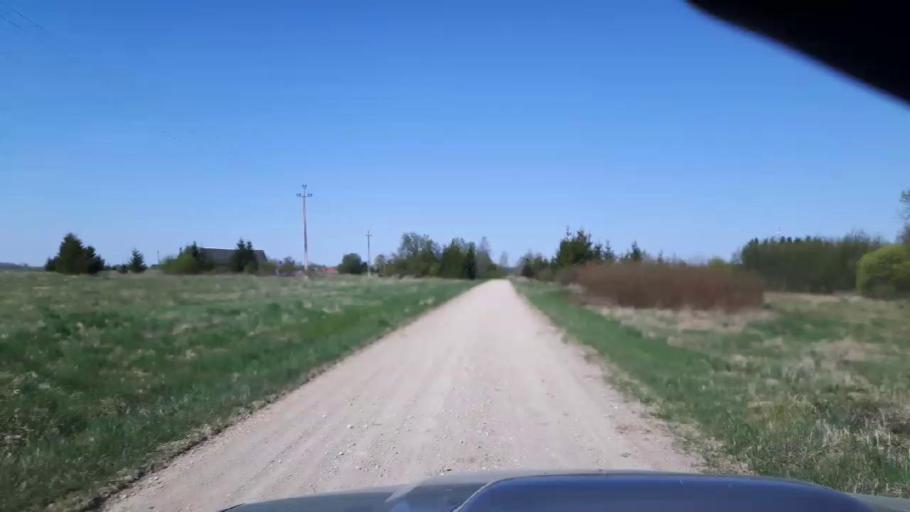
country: EE
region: Paernumaa
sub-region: Sindi linn
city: Sindi
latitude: 58.4444
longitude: 24.7845
